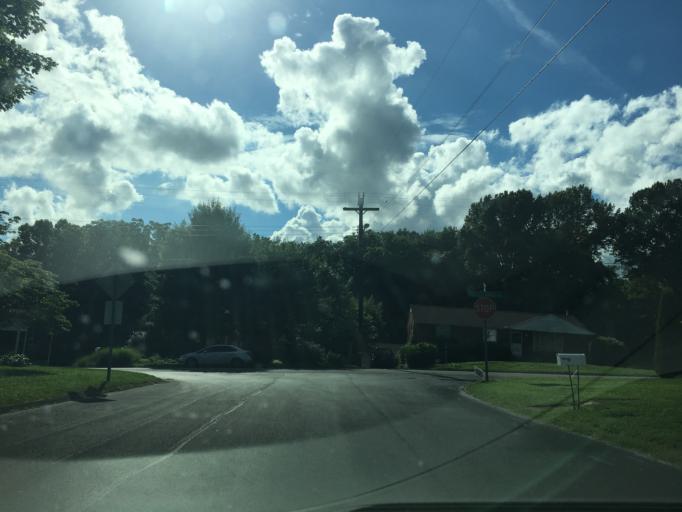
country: US
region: Tennessee
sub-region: Davidson County
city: Oak Hill
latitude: 36.0911
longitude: -86.7249
